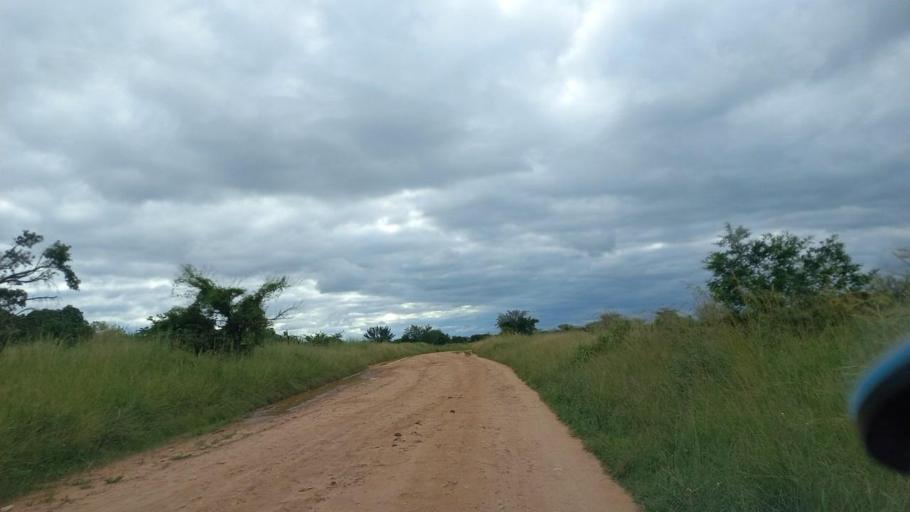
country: ZM
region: Lusaka
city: Chongwe
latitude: -15.4513
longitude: 28.8294
